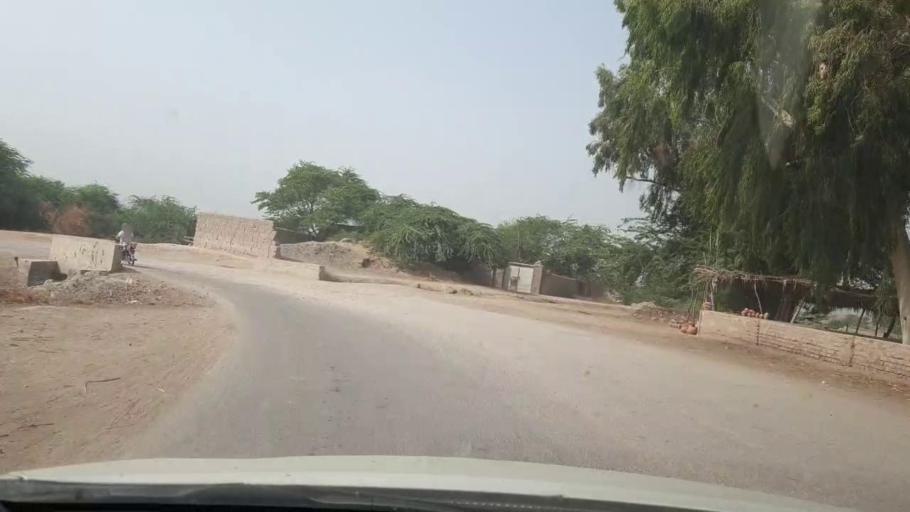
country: PK
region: Sindh
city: Kot Diji
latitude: 27.4331
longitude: 68.6508
